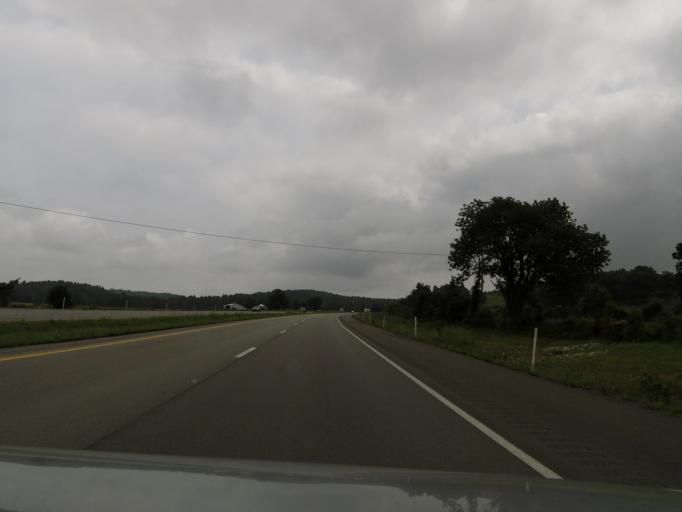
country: US
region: Kentucky
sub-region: Grayson County
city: Leitchfield
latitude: 37.4407
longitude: -86.3702
